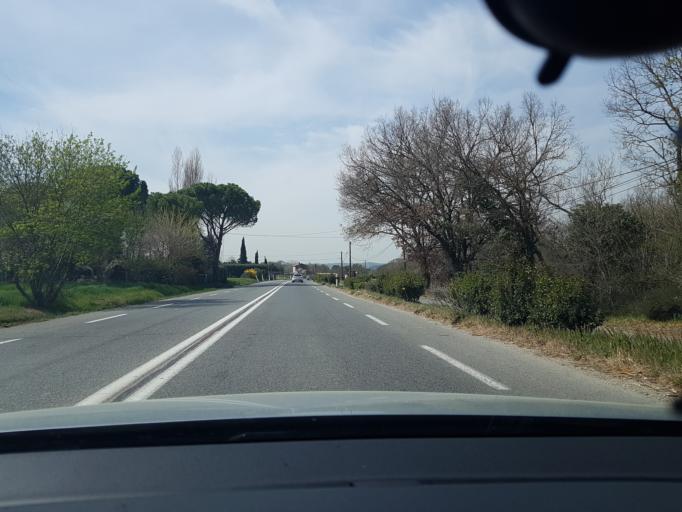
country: FR
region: Provence-Alpes-Cote d'Azur
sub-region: Departement des Bouches-du-Rhone
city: Chateauneuf-le-Rouge
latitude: 43.4725
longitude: 5.5802
